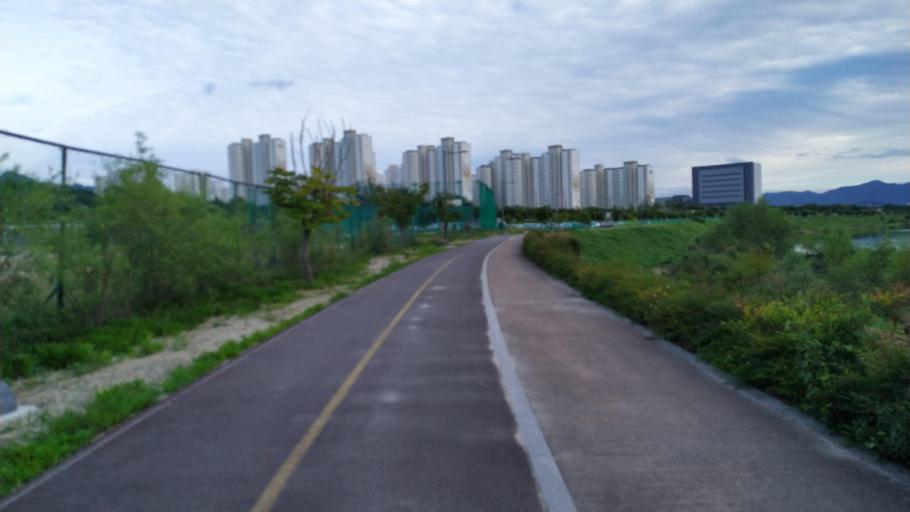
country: KR
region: Daegu
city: Daegu
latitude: 35.9290
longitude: 128.6304
